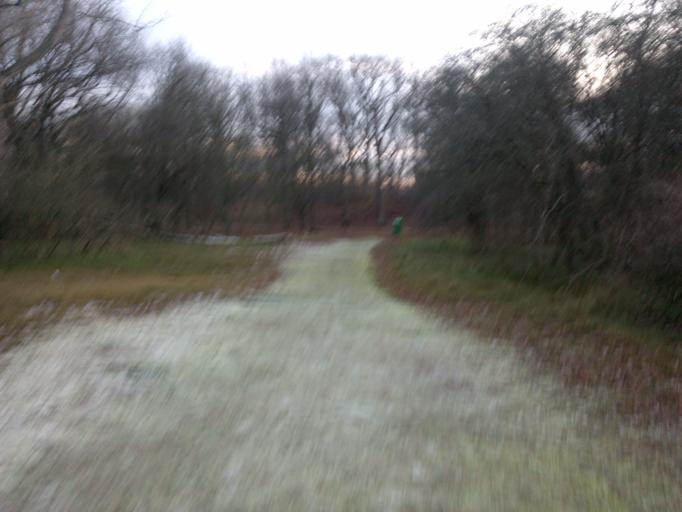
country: NL
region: South Holland
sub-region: Gemeente Leidschendam-Voorburg
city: Voorburg
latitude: 52.1295
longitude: 4.3367
